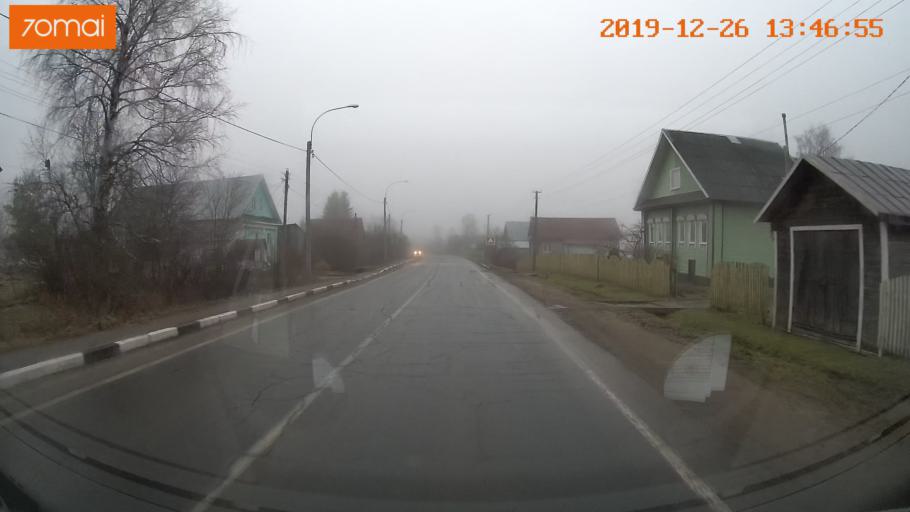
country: RU
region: Vologda
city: Sheksna
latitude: 58.6882
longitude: 38.5300
